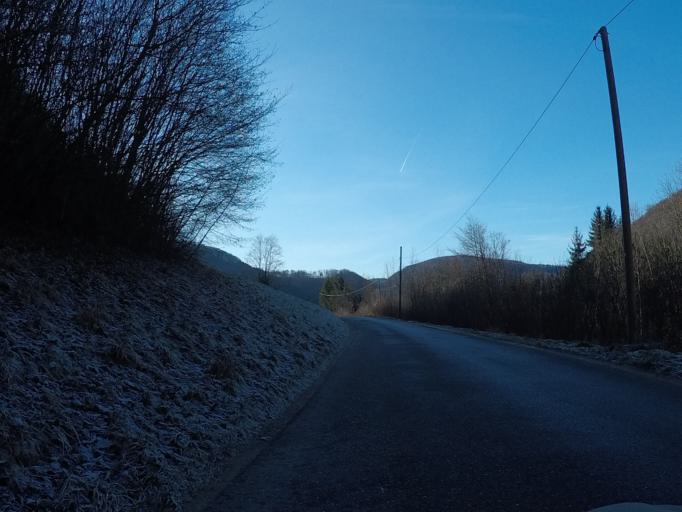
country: DE
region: Baden-Wuerttemberg
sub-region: Tuebingen Region
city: Eningen unter Achalm
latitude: 48.4468
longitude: 9.2793
